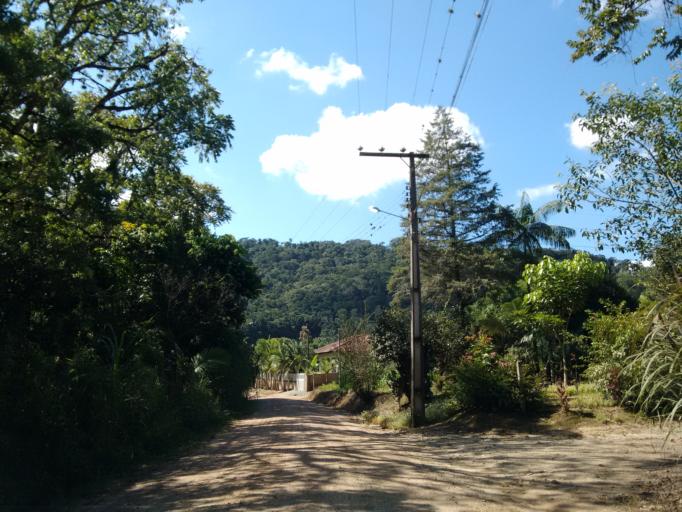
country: BR
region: Santa Catarina
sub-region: Indaial
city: Indaial
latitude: -26.9409
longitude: -49.1782
